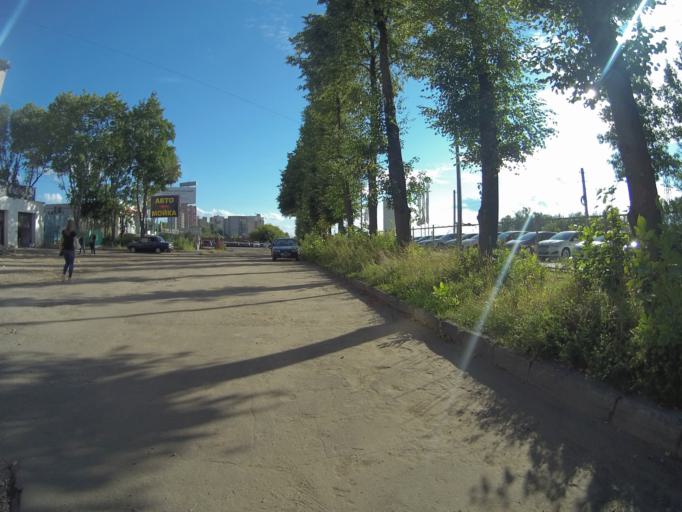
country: RU
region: Vladimir
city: Vladimir
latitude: 56.1576
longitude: 40.3749
